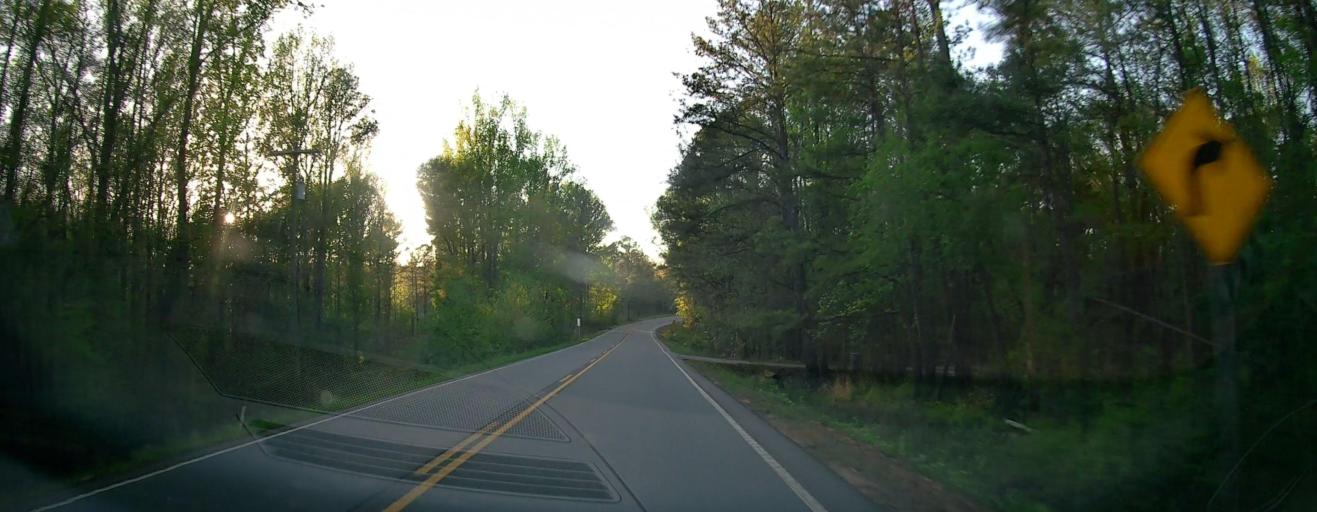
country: US
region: Georgia
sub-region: Talbot County
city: Talbotton
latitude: 32.5581
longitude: -84.5400
